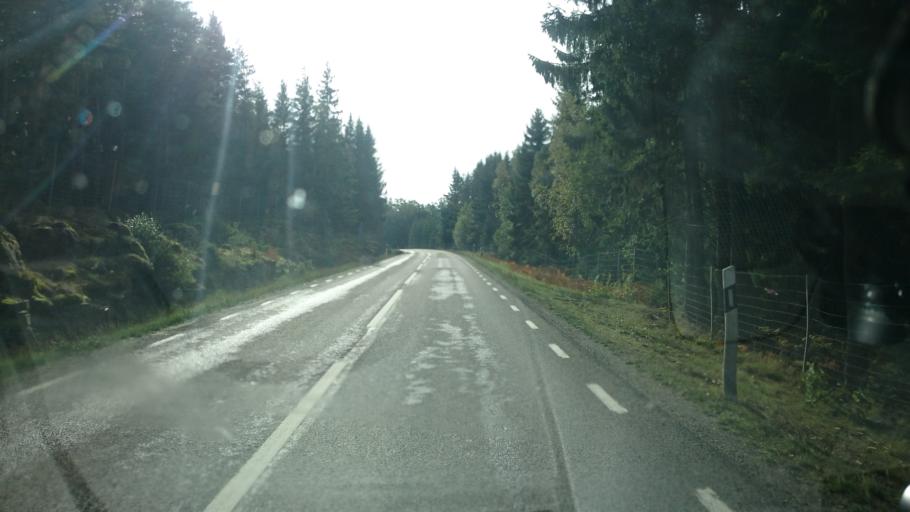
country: SE
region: Vaestra Goetaland
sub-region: Alingsas Kommun
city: Sollebrunn
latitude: 58.1429
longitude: 12.4201
